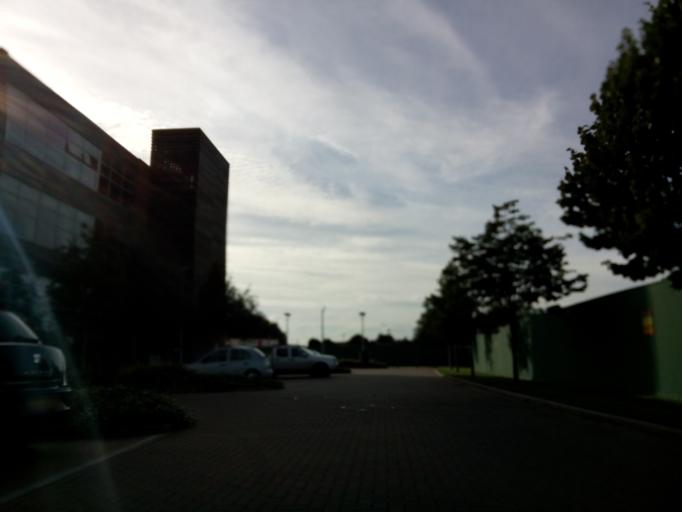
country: GB
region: England
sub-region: Norfolk
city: Thorpe Hamlet
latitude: 52.6354
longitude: 1.3053
